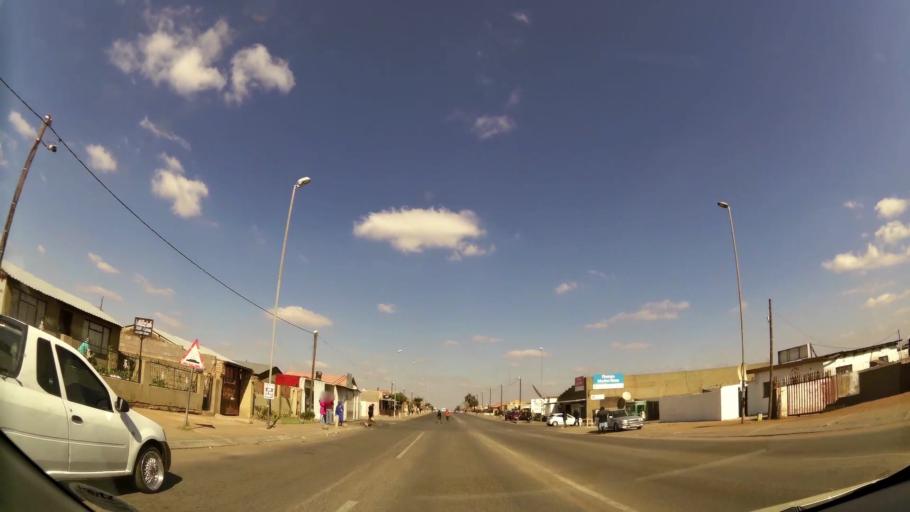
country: ZA
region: Gauteng
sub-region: West Rand District Municipality
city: Krugersdorp
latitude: -26.1546
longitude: 27.7854
